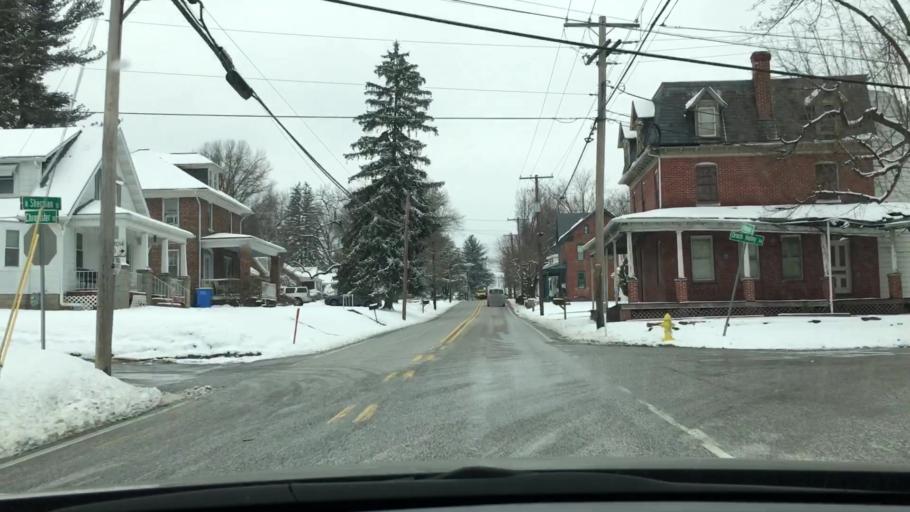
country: US
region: Pennsylvania
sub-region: York County
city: East York
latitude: 39.9950
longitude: -76.7064
